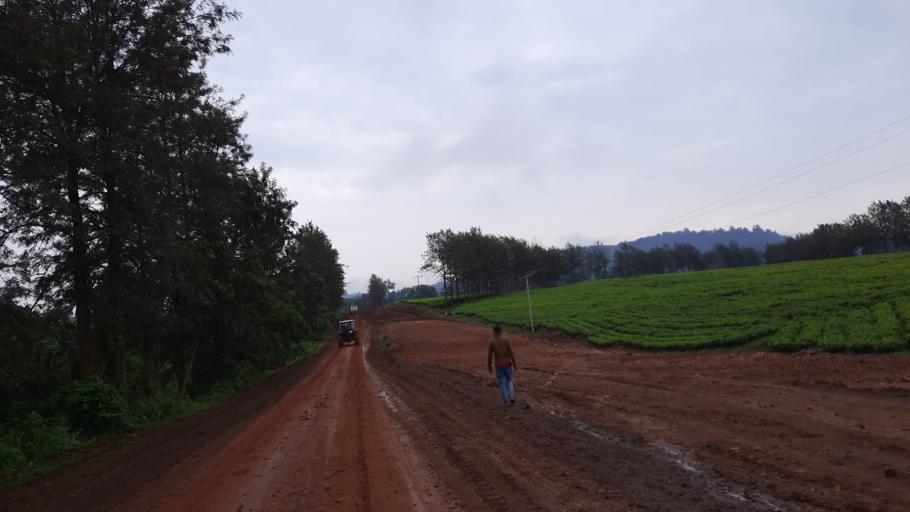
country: ET
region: Oromiya
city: Gore
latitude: 7.8585
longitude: 35.4762
